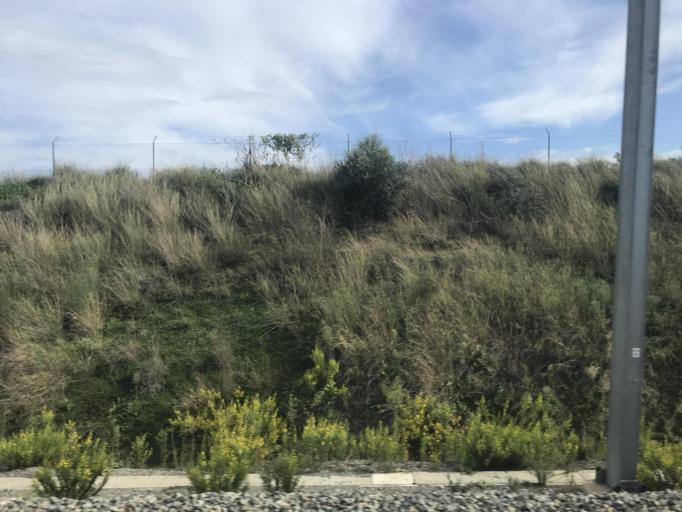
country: ES
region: Catalonia
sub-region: Provincia de Tarragona
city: Cambrils
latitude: 41.1013
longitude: 1.0963
